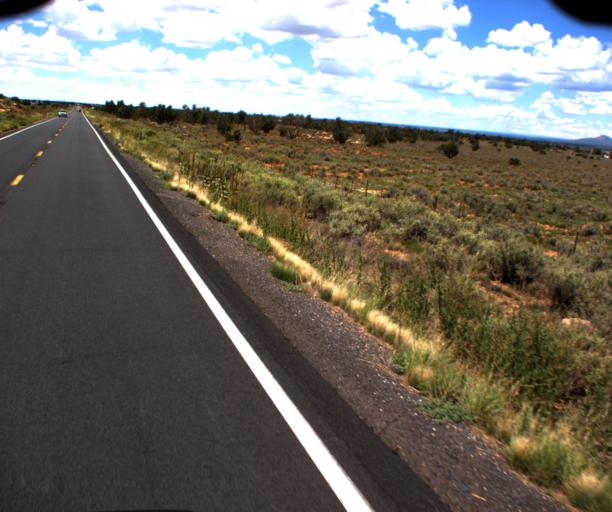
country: US
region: Arizona
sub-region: Coconino County
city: Williams
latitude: 35.6383
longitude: -112.1248
